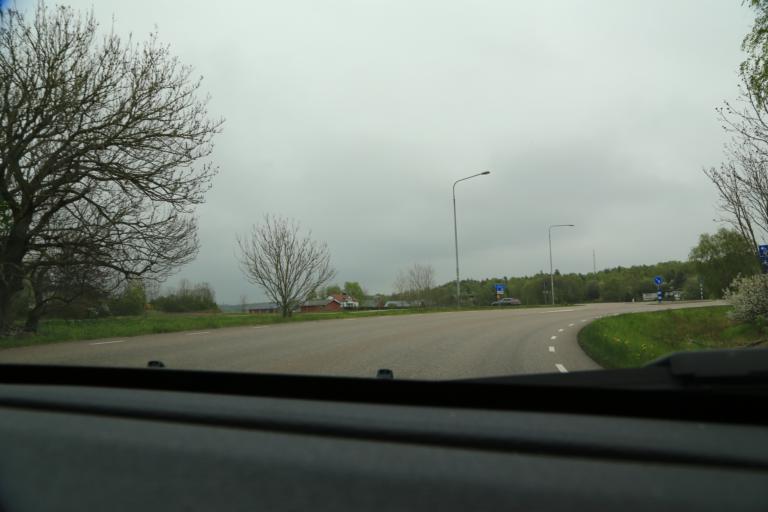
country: SE
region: Halland
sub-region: Kungsbacka Kommun
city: Frillesas
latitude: 57.2440
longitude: 12.1933
